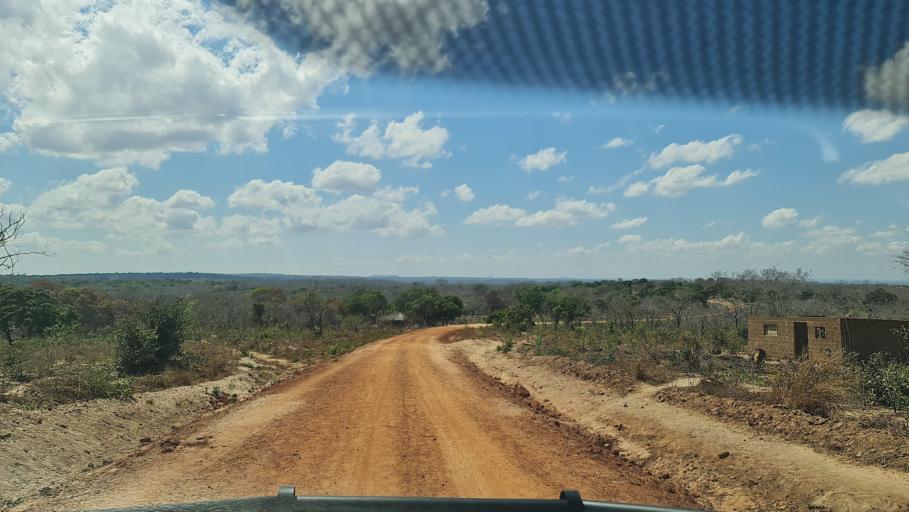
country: MZ
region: Nampula
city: Nacala
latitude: -14.1758
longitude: 40.2161
